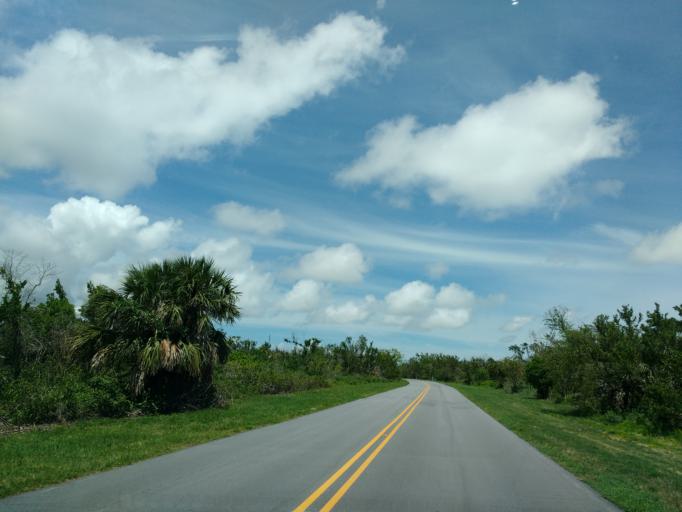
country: US
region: Florida
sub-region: Monroe County
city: Islamorada
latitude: 25.1390
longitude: -80.9332
